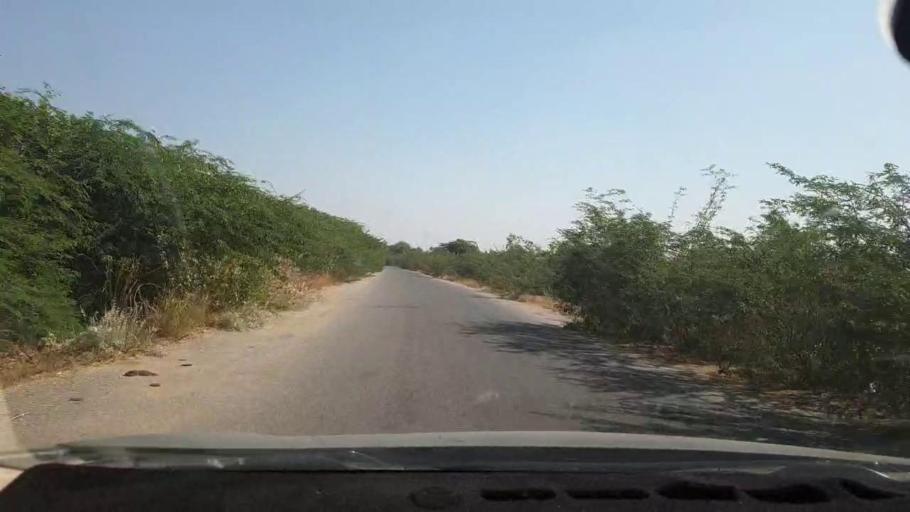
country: PK
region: Sindh
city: Malir Cantonment
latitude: 25.1421
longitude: 67.1954
